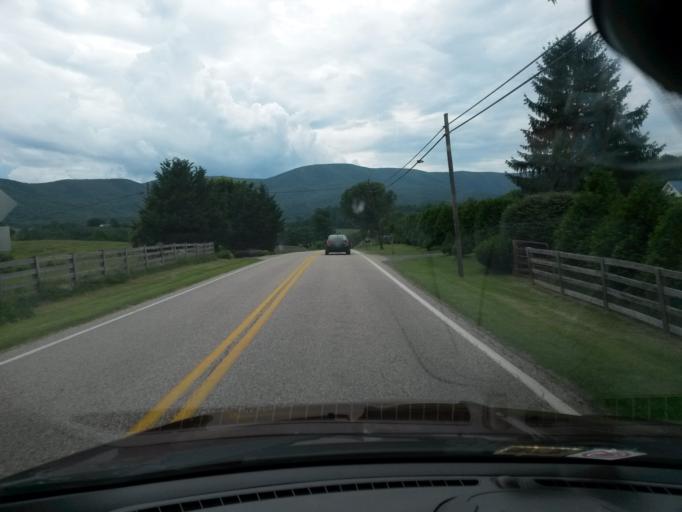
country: US
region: Virginia
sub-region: Alleghany County
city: Clifton Forge
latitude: 37.8859
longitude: -79.9106
